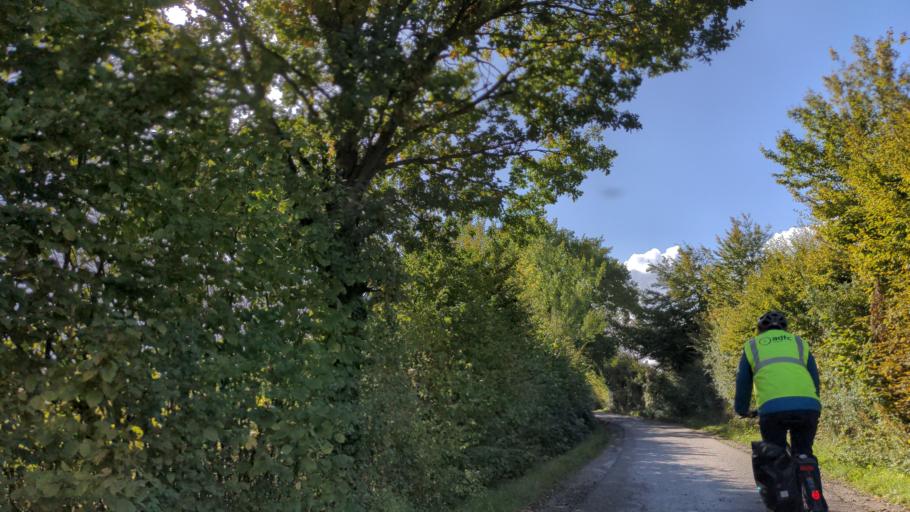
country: DE
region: Schleswig-Holstein
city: Heidekamp
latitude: 53.8344
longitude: 10.5161
